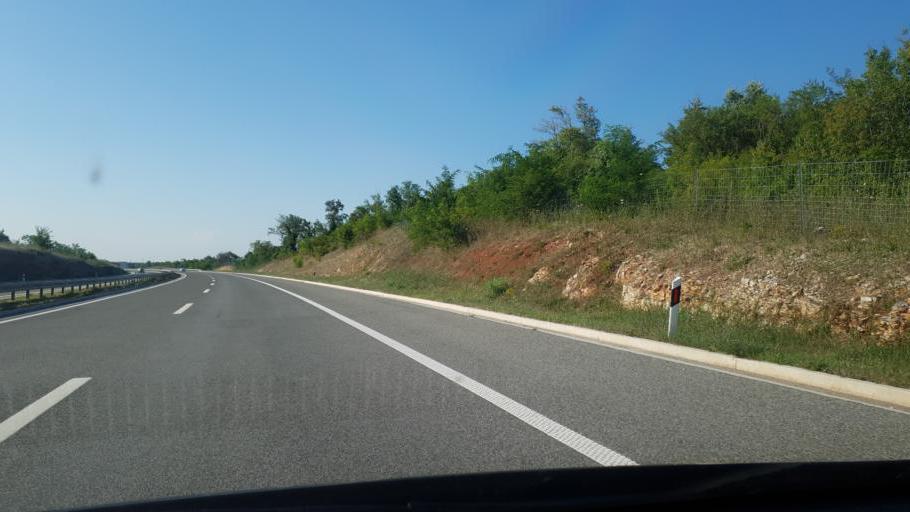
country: HR
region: Istarska
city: Vodnjan
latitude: 44.9710
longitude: 13.8725
